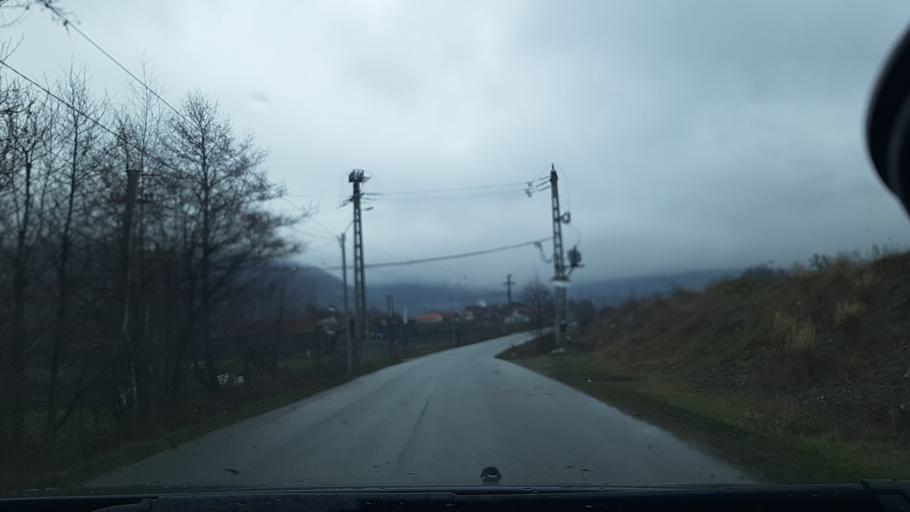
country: RO
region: Hunedoara
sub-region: Oras Petrila
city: Petrila
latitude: 45.4343
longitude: 23.4186
